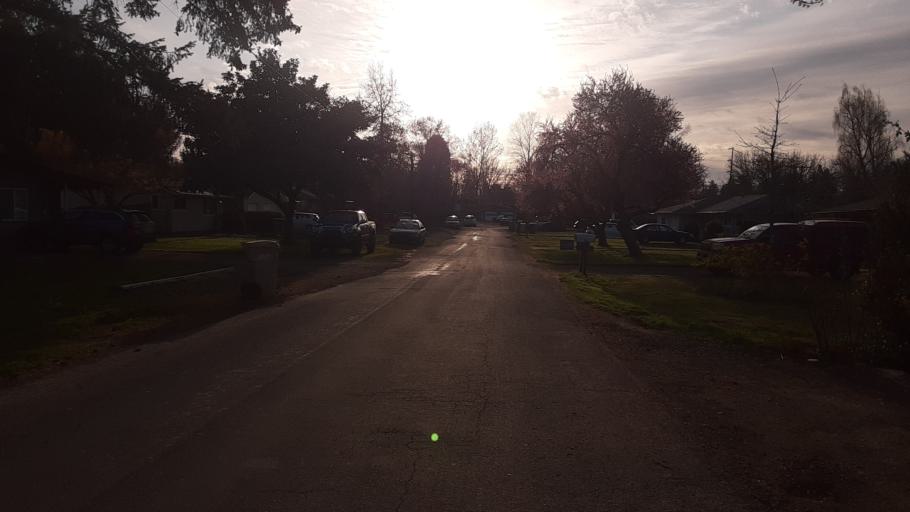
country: US
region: Oregon
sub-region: Benton County
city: Corvallis
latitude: 44.5494
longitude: -123.2623
